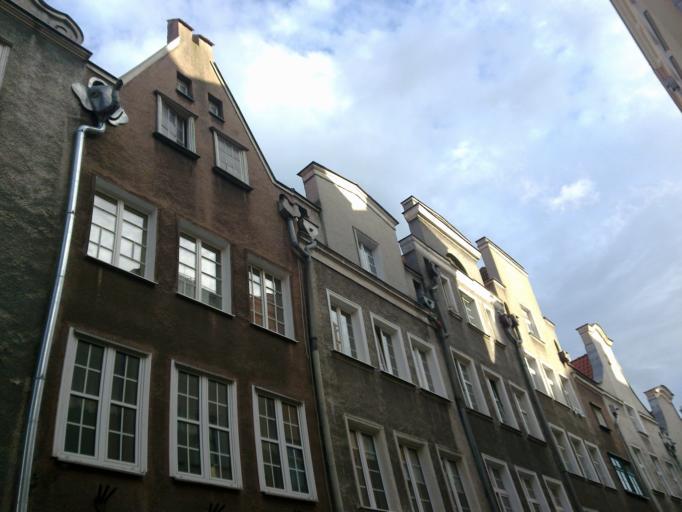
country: PL
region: Pomeranian Voivodeship
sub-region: Gdansk
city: Gdansk
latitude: 54.3480
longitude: 18.6553
